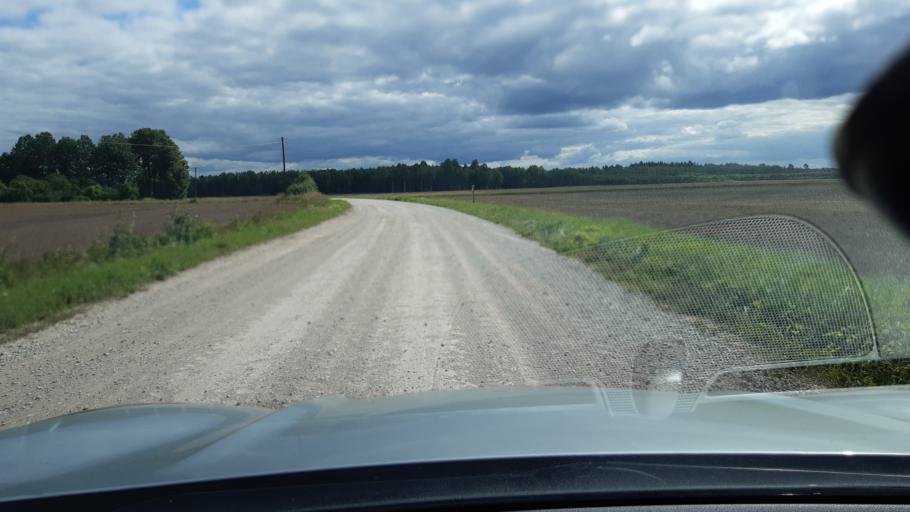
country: EE
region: Raplamaa
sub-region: Jaervakandi vald
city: Jarvakandi
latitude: 58.7936
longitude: 24.9787
